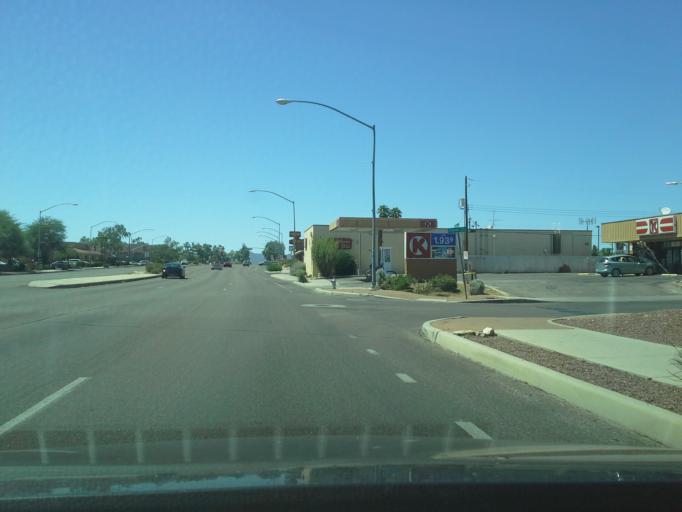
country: US
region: Arizona
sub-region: Pima County
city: Tucson
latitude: 32.2362
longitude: -110.9243
